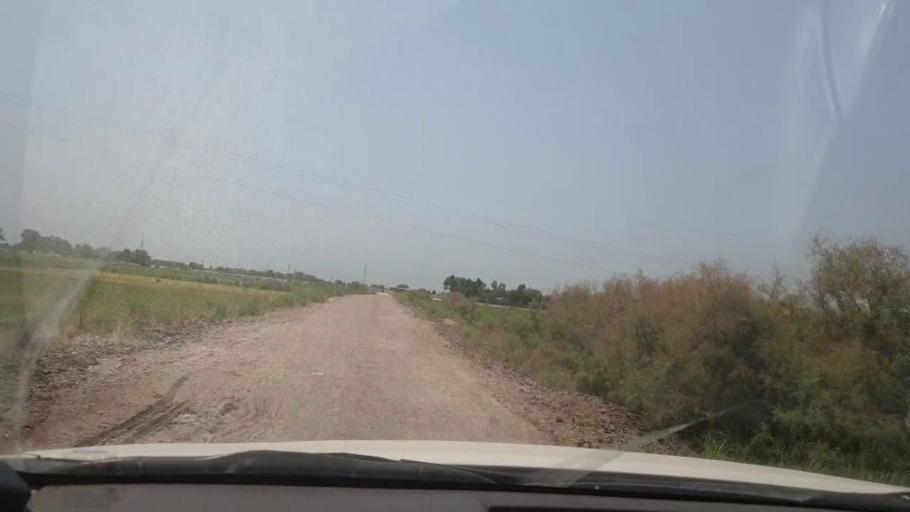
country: PK
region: Sindh
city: Lakhi
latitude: 27.8718
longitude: 68.6938
